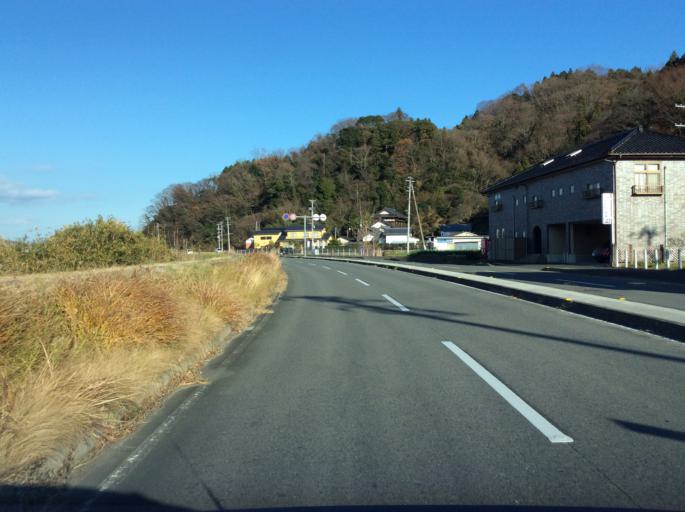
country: JP
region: Fukushima
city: Iwaki
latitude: 37.0471
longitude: 140.9108
